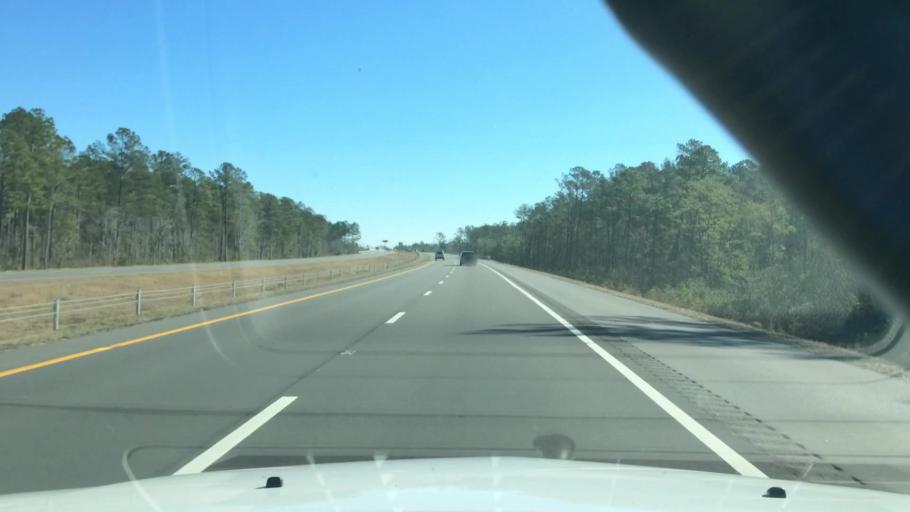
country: US
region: North Carolina
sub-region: Brunswick County
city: Leland
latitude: 34.2731
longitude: -78.0292
